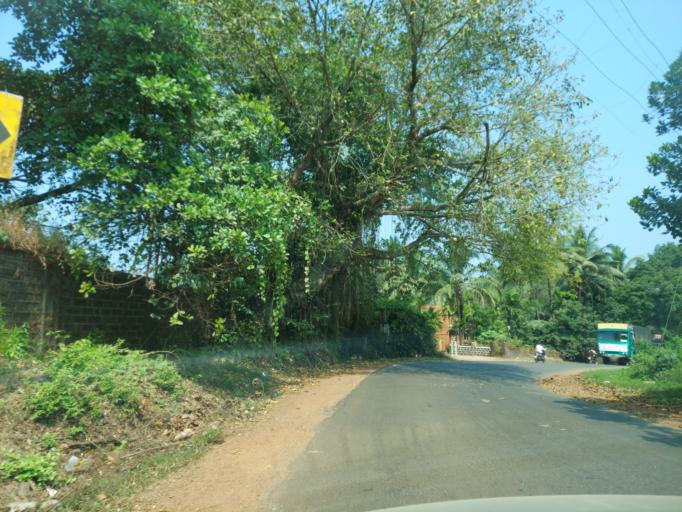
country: IN
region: Maharashtra
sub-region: Sindhudurg
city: Kudal
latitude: 16.0002
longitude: 73.6857
